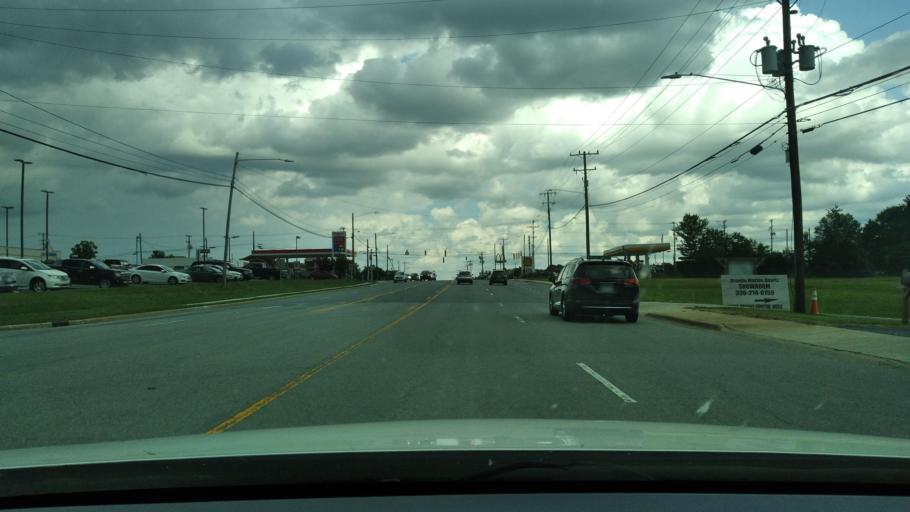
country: US
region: North Carolina
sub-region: Alamance County
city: Elon
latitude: 36.0803
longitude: -79.5157
